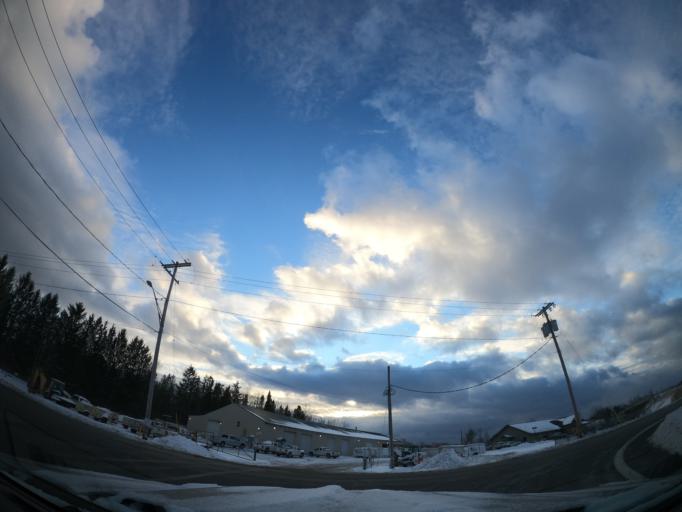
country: US
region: New York
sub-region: Onondaga County
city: Brewerton
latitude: 43.2164
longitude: -76.1271
